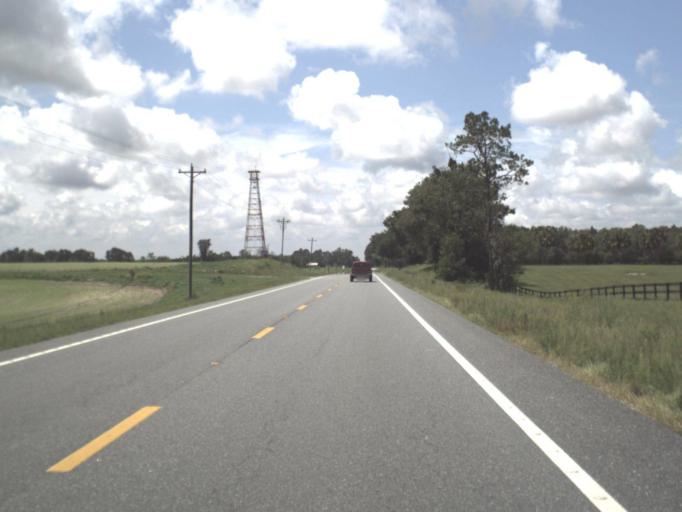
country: US
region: Florida
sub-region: Gilchrist County
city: Trenton
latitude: 29.8299
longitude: -82.8673
